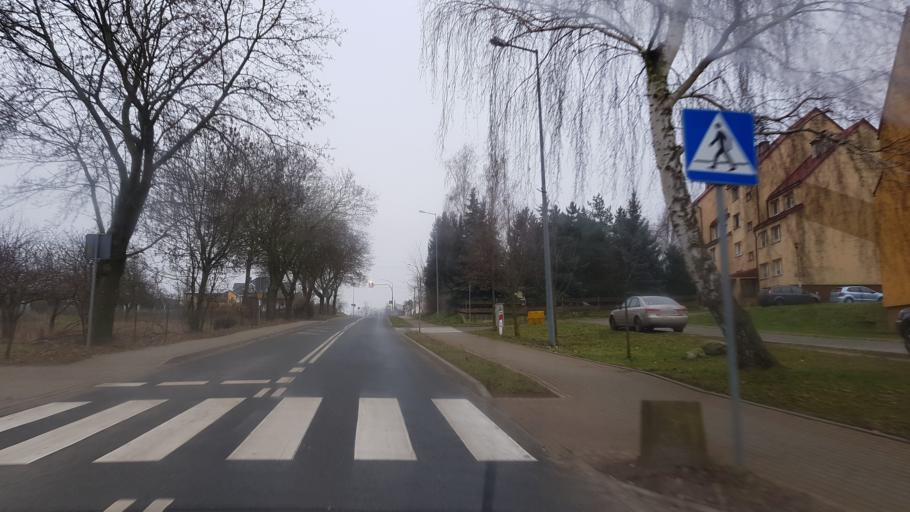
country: PL
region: West Pomeranian Voivodeship
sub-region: Powiat gryfinski
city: Cedynia
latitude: 52.8796
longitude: 14.2134
